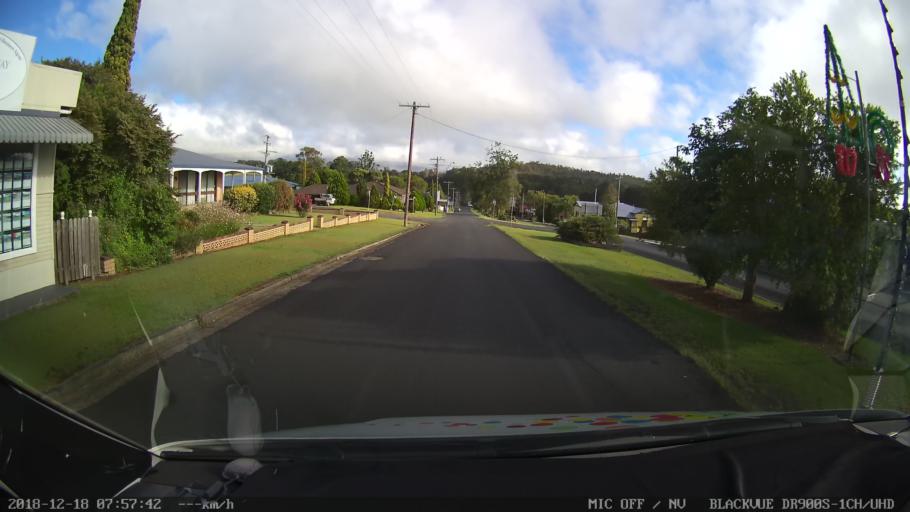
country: AU
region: New South Wales
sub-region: Kyogle
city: Kyogle
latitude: -28.3920
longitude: 152.6118
